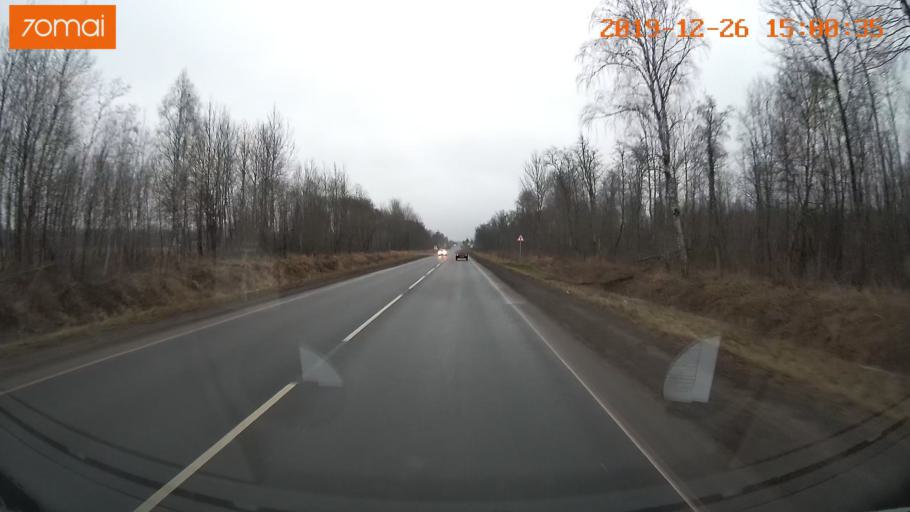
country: RU
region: Jaroslavl
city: Rybinsk
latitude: 58.2448
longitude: 38.8540
